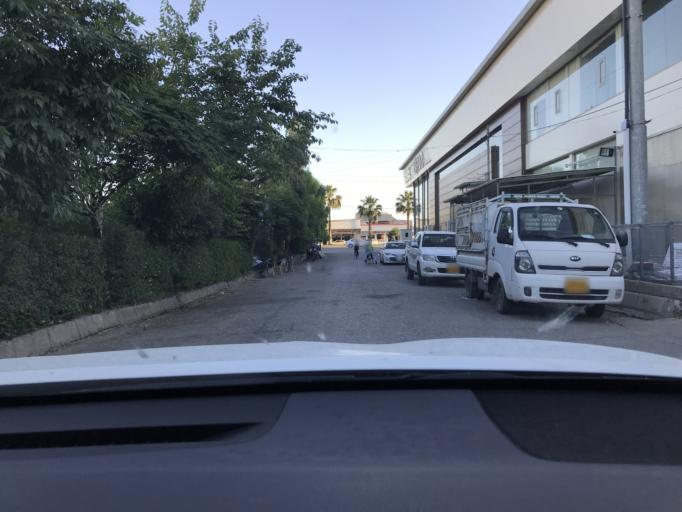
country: IQ
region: Arbil
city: Erbil
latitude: 36.2044
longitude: 44.0128
